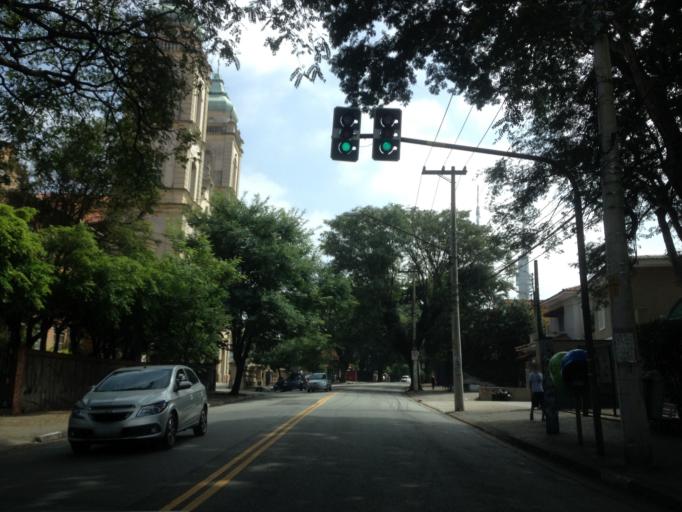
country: BR
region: Sao Paulo
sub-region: Sao Paulo
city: Sao Paulo
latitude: -23.5490
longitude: -46.6805
